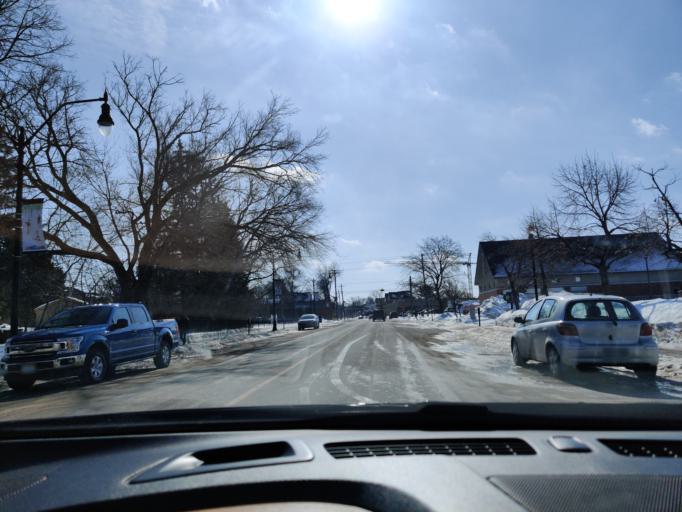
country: CA
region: Ontario
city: Collingwood
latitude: 44.5000
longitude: -80.2153
